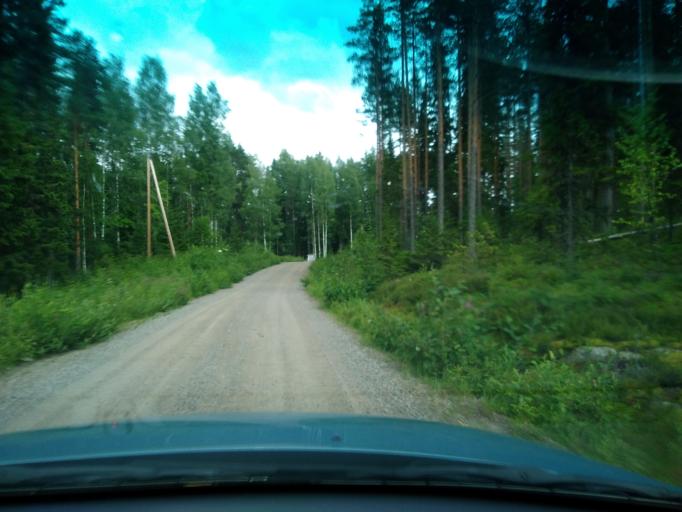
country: FI
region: Central Finland
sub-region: Saarijaervi-Viitasaari
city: Pylkoenmaeki
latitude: 62.7614
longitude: 24.9772
